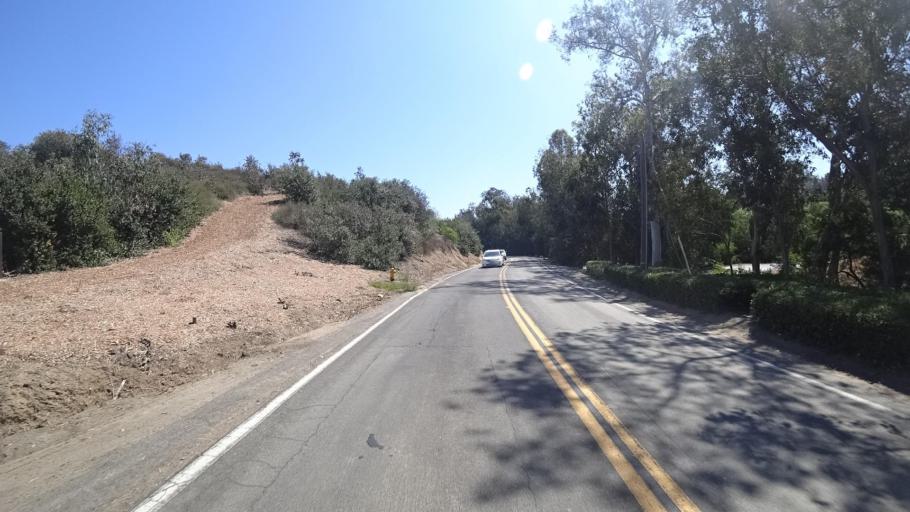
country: US
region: California
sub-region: San Diego County
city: Rancho Santa Fe
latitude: 33.0103
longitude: -117.2274
